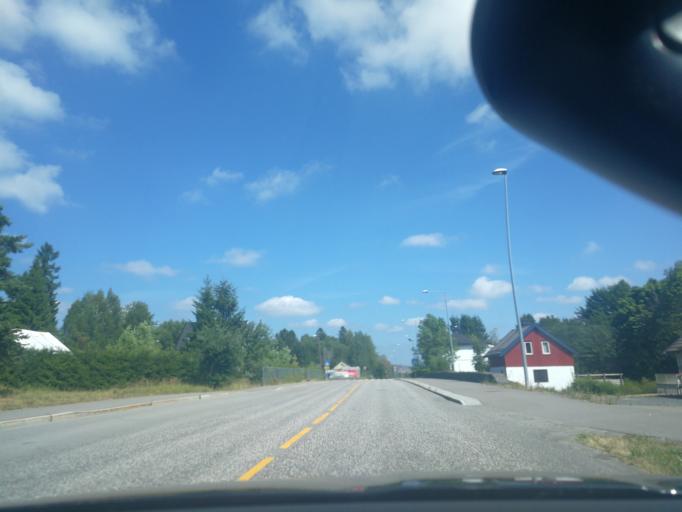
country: NO
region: Vestfold
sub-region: Stokke
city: Stokke
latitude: 59.2031
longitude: 10.2366
